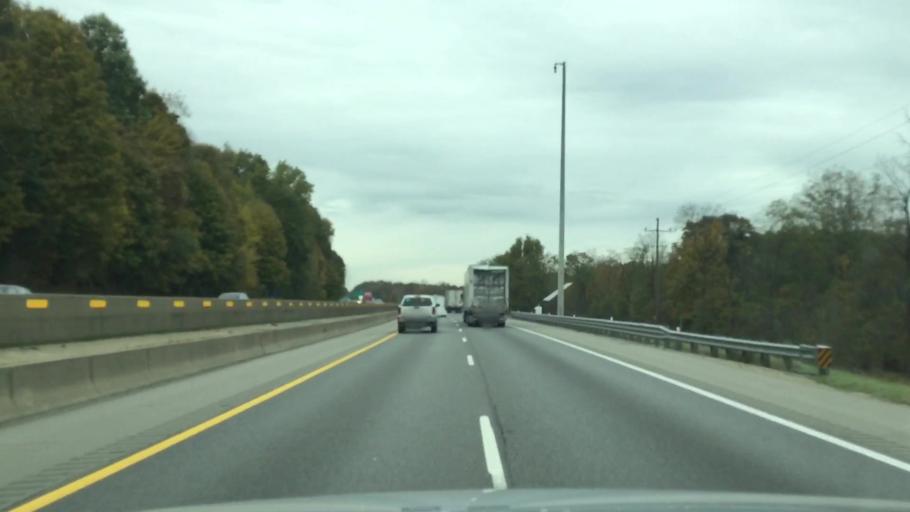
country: US
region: Michigan
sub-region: Kalamazoo County
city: Galesburg
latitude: 42.2708
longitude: -85.4776
